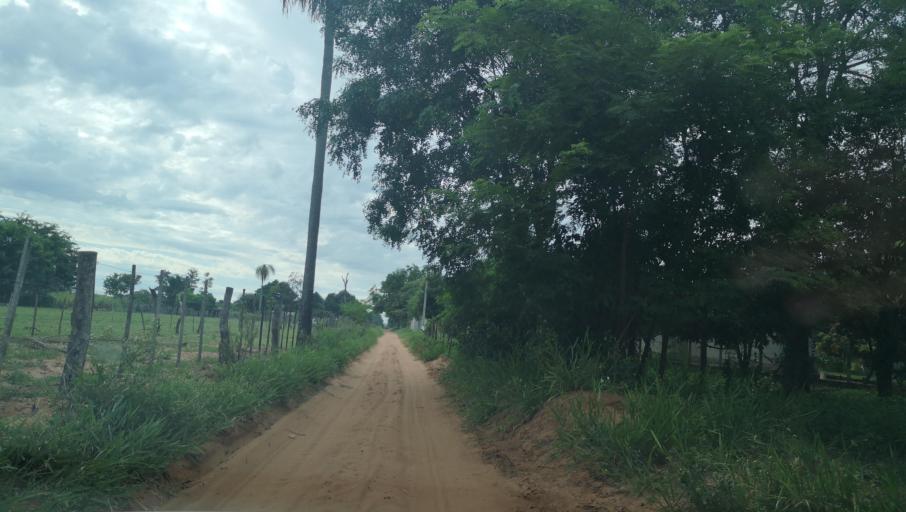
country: PY
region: San Pedro
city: Capiibary
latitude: -24.7435
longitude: -56.0289
